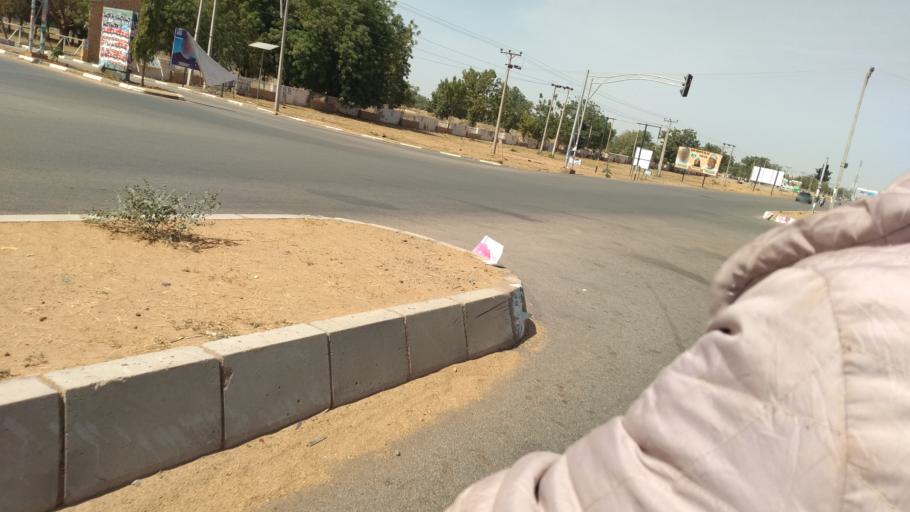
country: NG
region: Jigawa
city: Dutse
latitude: 11.6848
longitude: 9.3395
